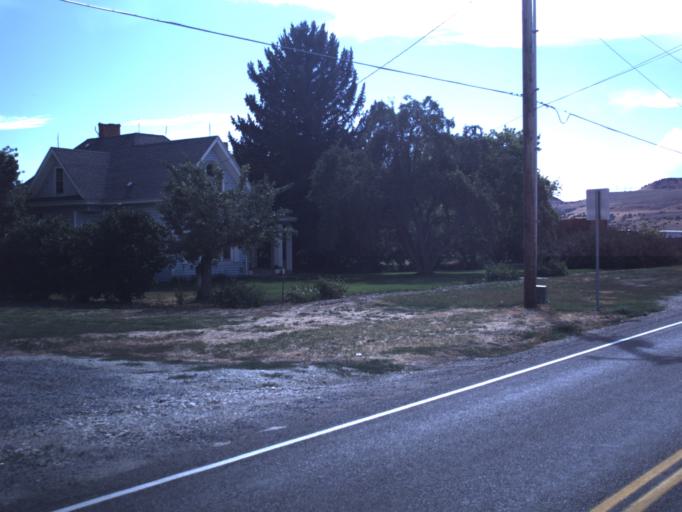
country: US
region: Utah
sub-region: Cache County
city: Benson
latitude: 41.8626
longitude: -111.9981
